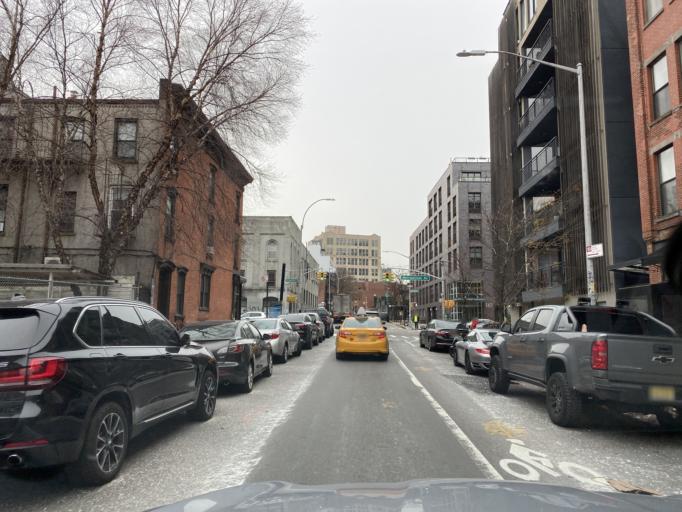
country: US
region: New York
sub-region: Queens County
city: Long Island City
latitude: 40.7171
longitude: -73.9630
